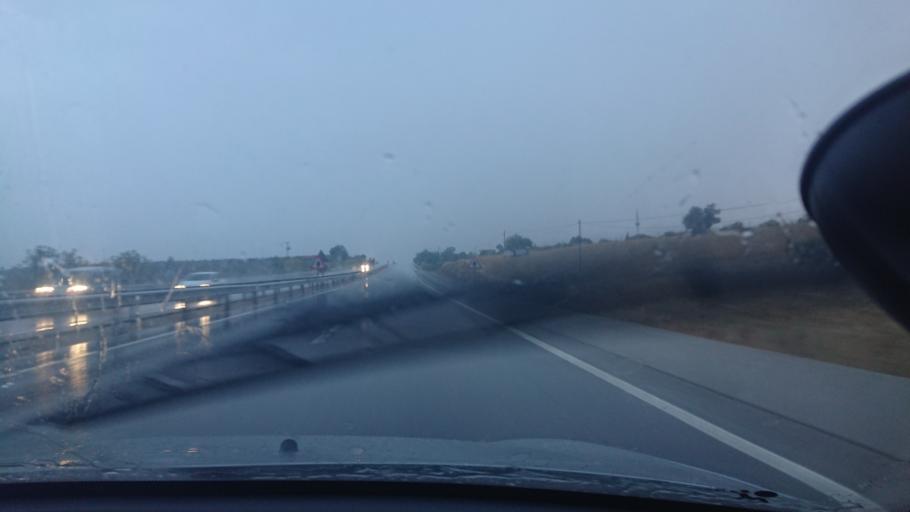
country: TR
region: Manisa
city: Menye
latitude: 38.5319
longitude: 28.4072
